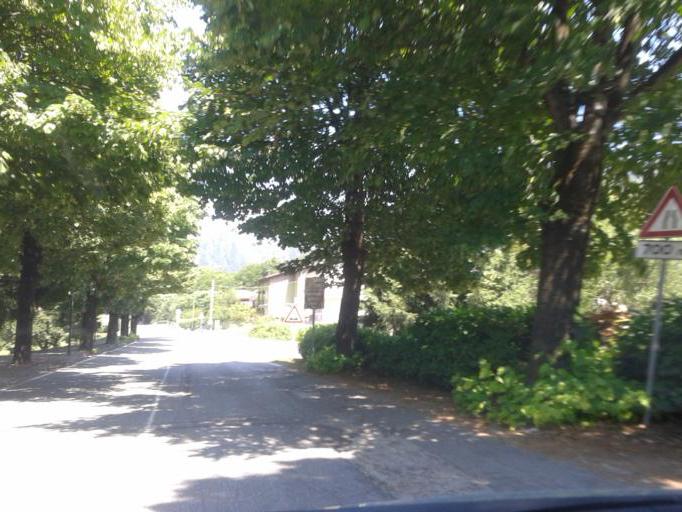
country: IT
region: Lombardy
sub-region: Provincia di Brescia
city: Idro
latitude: 45.7332
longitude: 10.4597
